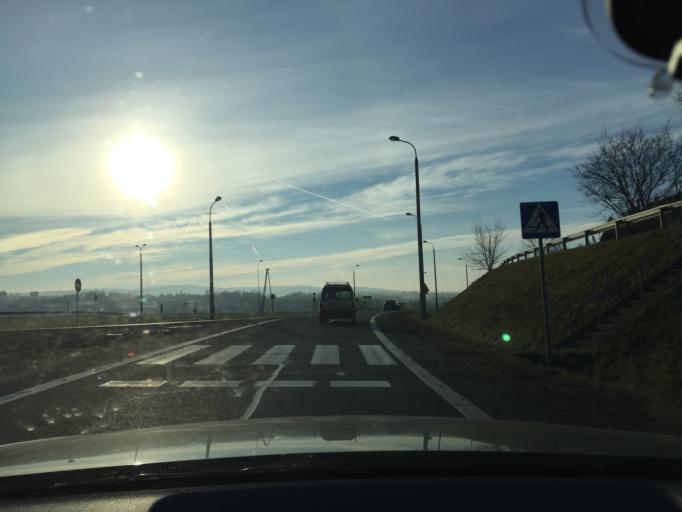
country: PL
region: Lesser Poland Voivodeship
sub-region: Powiat myslenicki
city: Glogoczow
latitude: 49.9084
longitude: 19.8682
